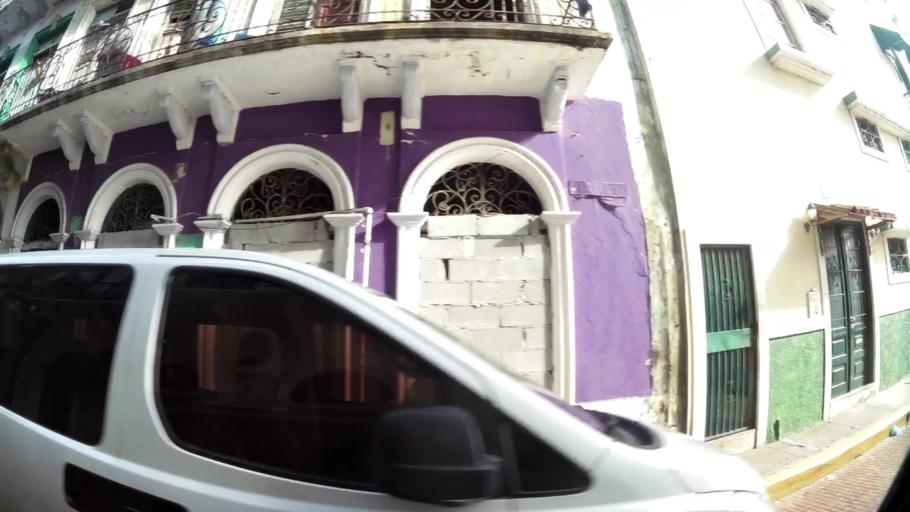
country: PA
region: Panama
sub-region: Distrito de Panama
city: Ancon
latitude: 8.9513
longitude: -79.5326
